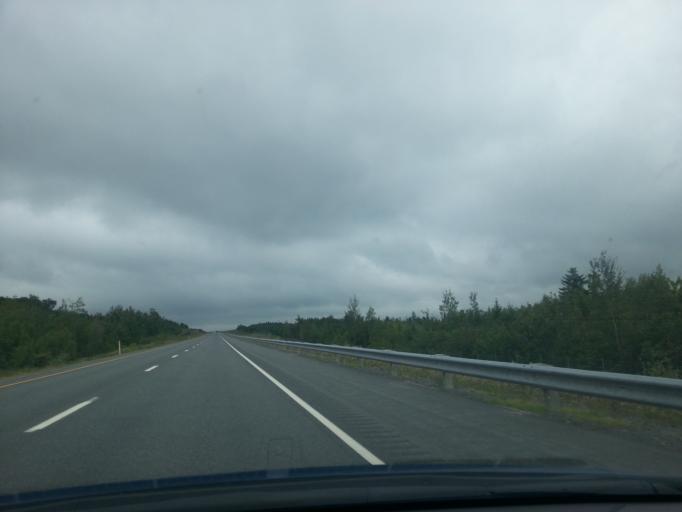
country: CA
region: New Brunswick
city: Nackawic
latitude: 45.9192
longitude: -67.1444
